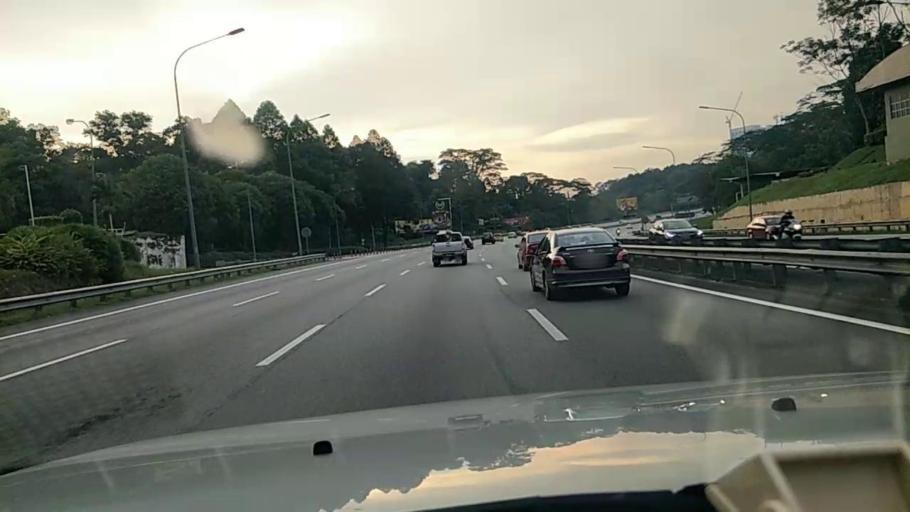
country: MY
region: Selangor
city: Kampung Baru Subang
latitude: 3.1886
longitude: 101.5859
